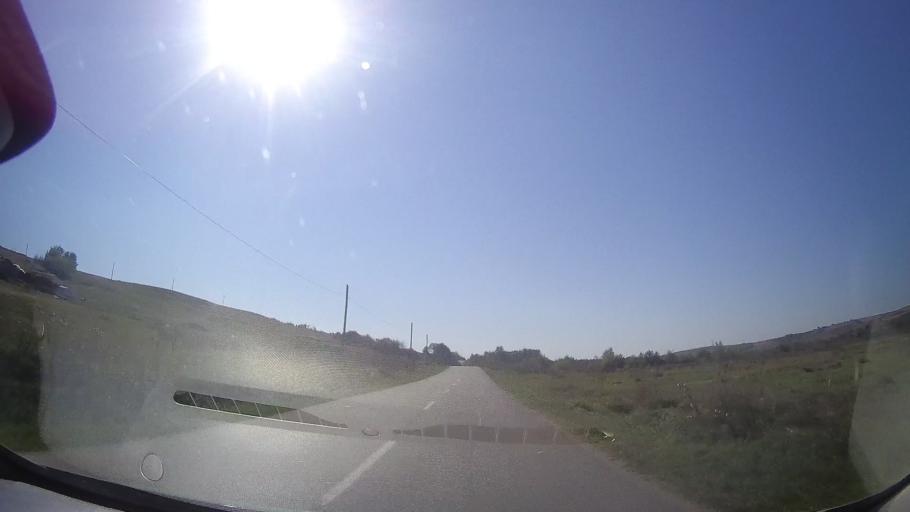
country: RO
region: Timis
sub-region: Comuna Bethausen
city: Bethausen
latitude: 45.8567
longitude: 21.9675
